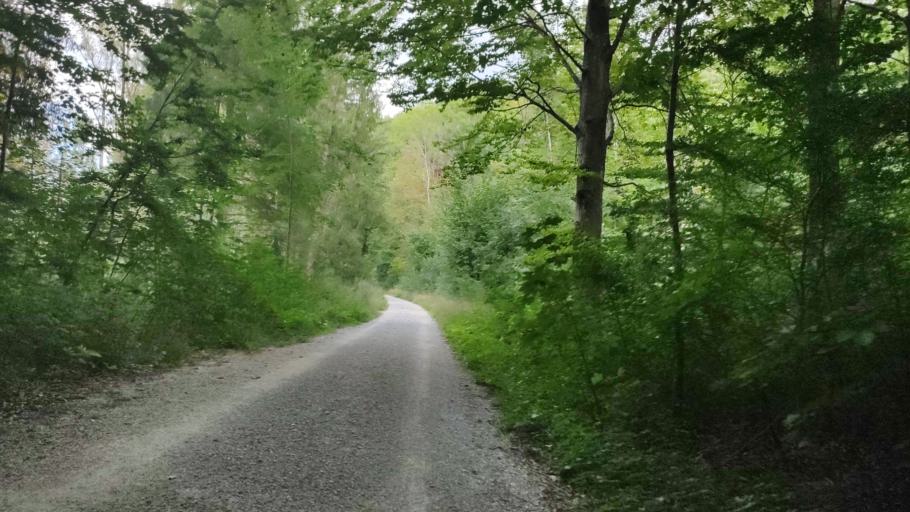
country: DE
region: Bavaria
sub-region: Upper Bavaria
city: Scheuring
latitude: 48.1430
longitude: 10.8671
